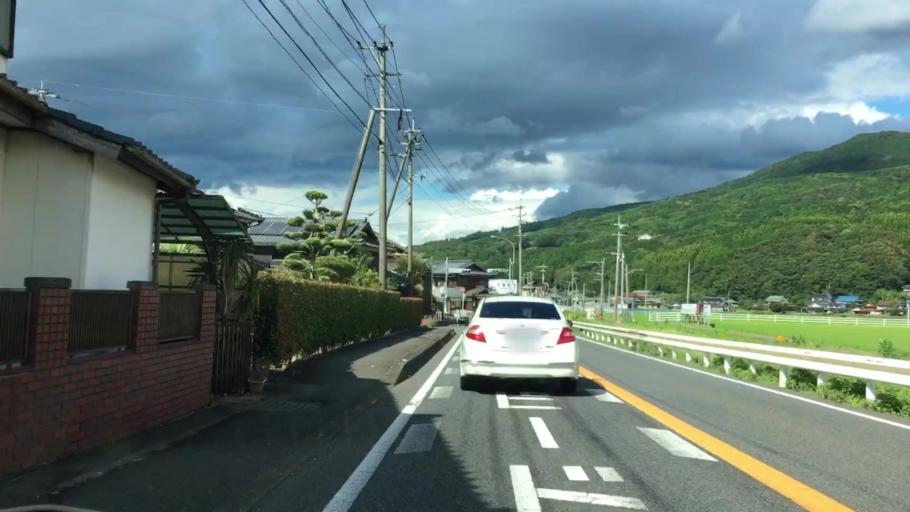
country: JP
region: Saga Prefecture
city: Imaricho-ko
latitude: 33.2281
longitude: 129.8483
